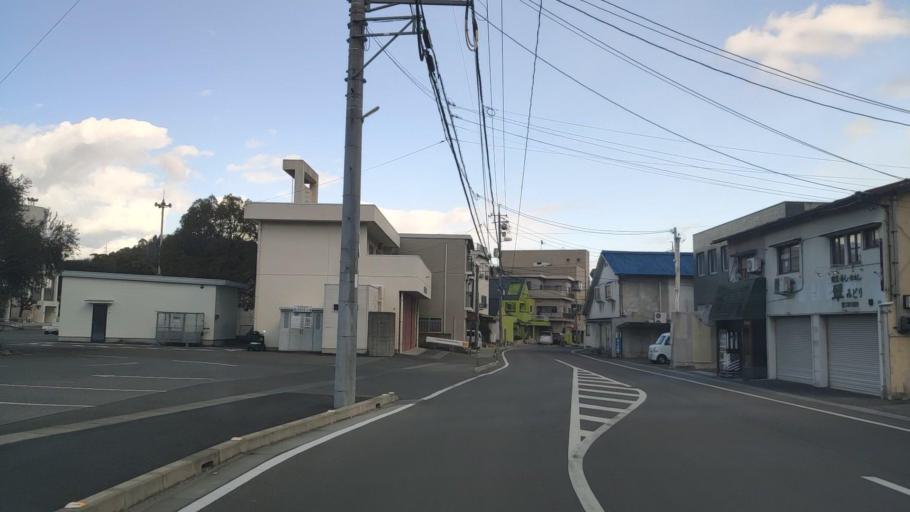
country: JP
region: Hiroshima
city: Innoshima
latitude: 34.2042
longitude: 133.1128
